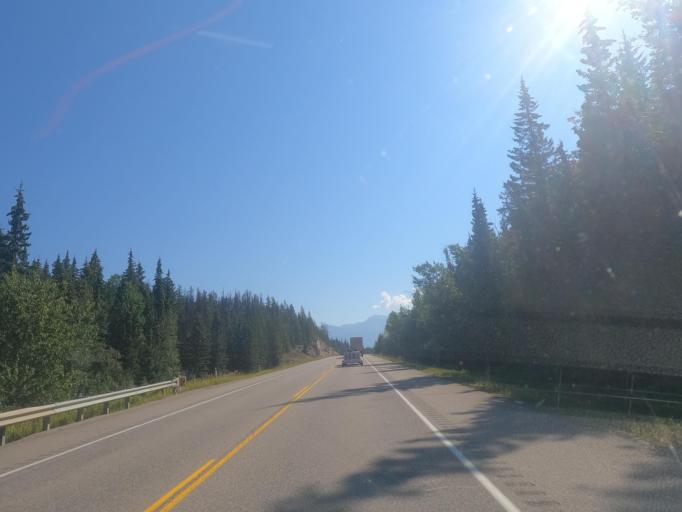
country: CA
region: Alberta
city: Jasper Park Lodge
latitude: 52.8606
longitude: -118.1845
